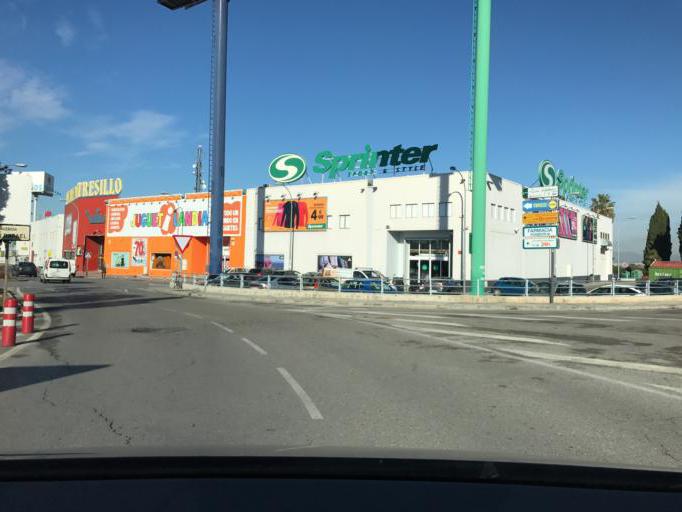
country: ES
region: Andalusia
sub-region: Provincia de Granada
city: Armilla
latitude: 37.1534
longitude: -3.6136
